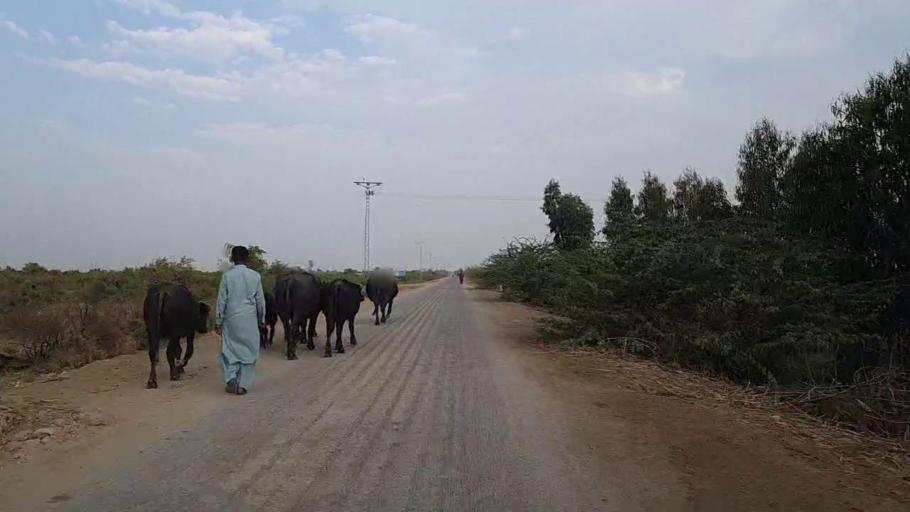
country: PK
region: Sindh
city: Samaro
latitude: 25.3828
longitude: 69.3310
